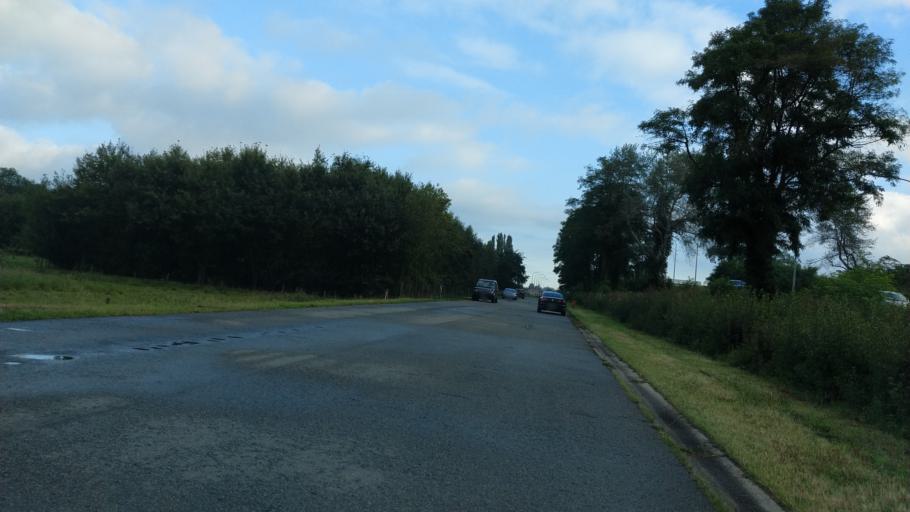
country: BE
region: Flanders
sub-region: Provincie Oost-Vlaanderen
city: Lovendegem
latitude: 51.0900
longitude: 3.6374
